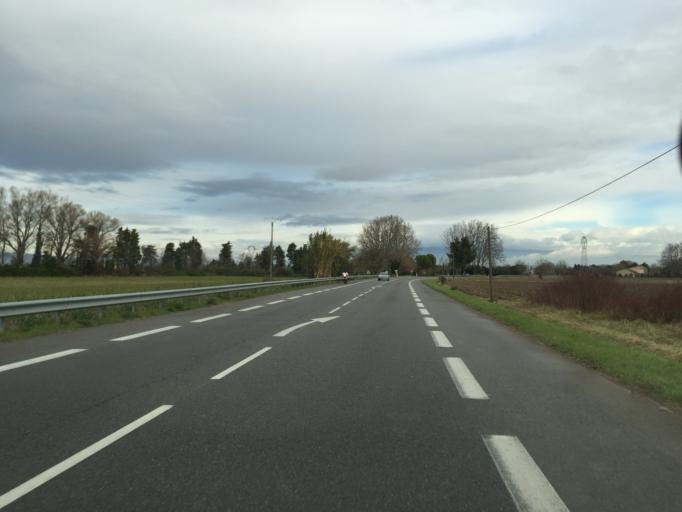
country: FR
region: Provence-Alpes-Cote d'Azur
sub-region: Departement du Vaucluse
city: Velleron
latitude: 43.9772
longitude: 4.9987
